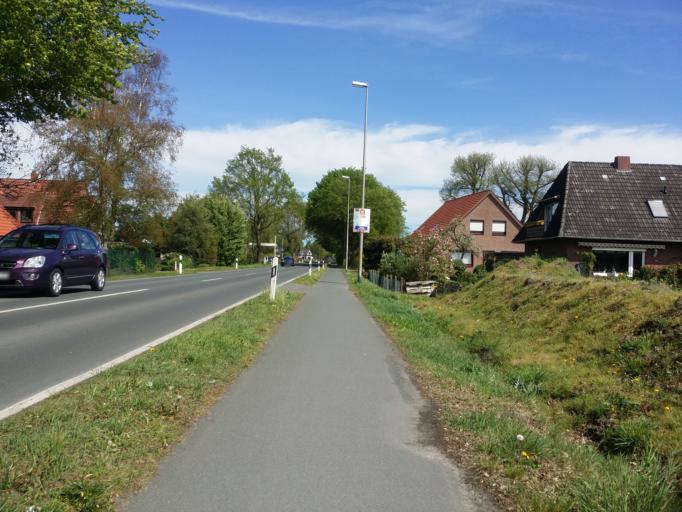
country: DE
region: Lower Saxony
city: Delmenhorst
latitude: 53.0828
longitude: 8.6474
